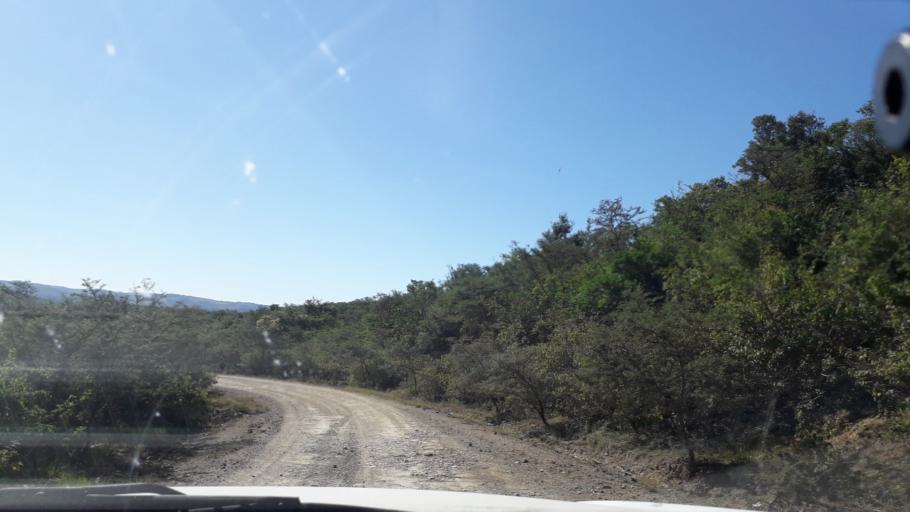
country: ZA
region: Eastern Cape
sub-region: Amathole District Municipality
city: Komga
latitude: -32.7768
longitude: 27.9592
